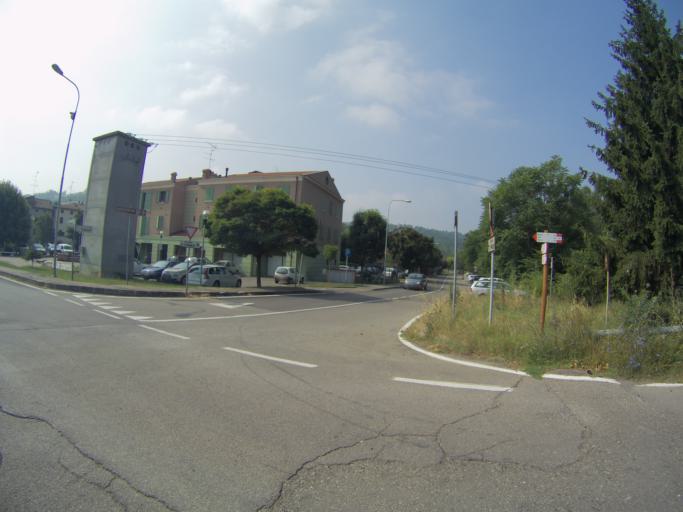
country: IT
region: Emilia-Romagna
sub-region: Provincia di Reggio Emilia
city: Ventoso
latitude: 44.5880
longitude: 10.6728
